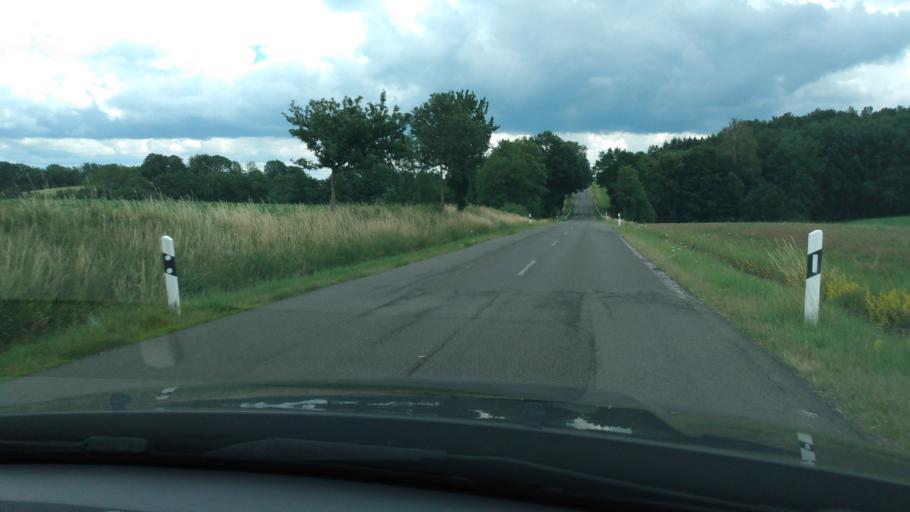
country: DE
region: Rheinland-Pfalz
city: Karl
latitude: 50.0522
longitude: 6.7904
